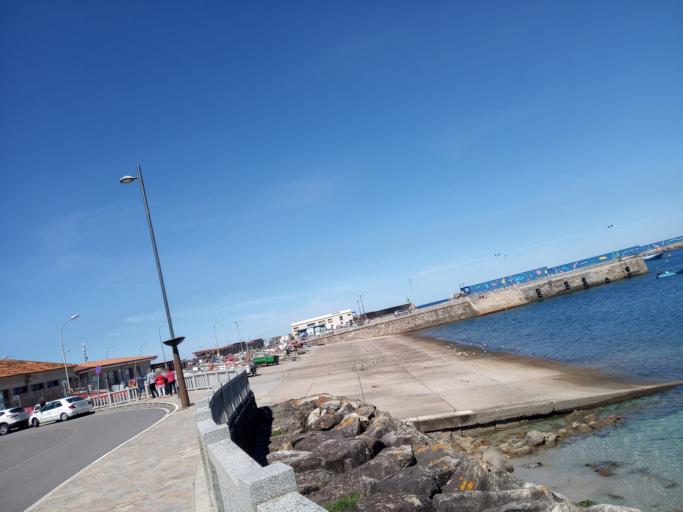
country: ES
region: Galicia
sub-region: Provincia de Pontevedra
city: A Guarda
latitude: 41.8984
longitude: -8.8756
